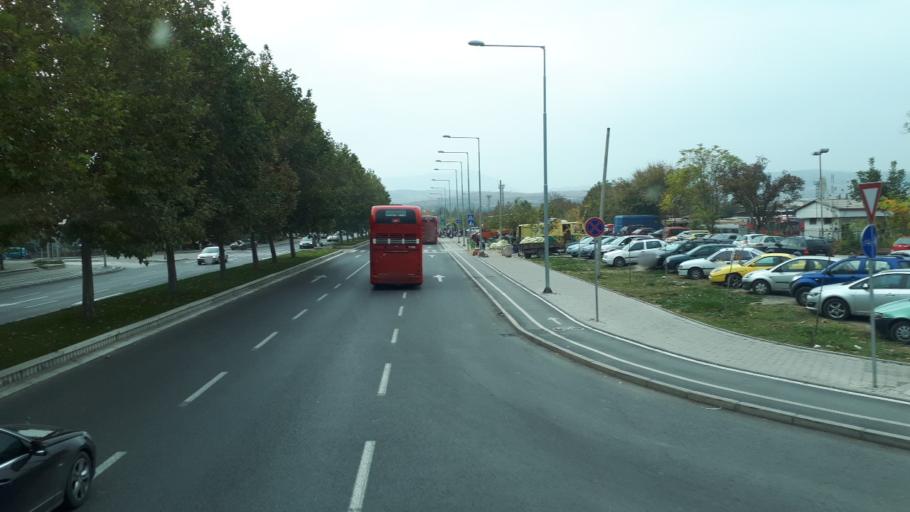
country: MK
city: Krushopek
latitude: 42.0093
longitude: 21.3666
